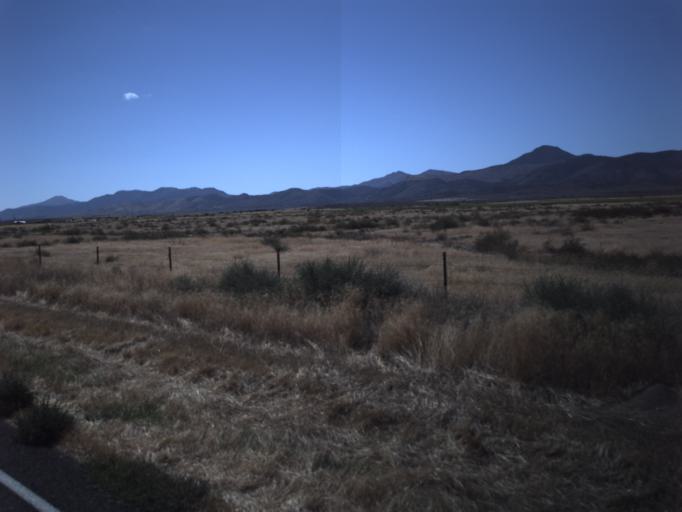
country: US
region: Utah
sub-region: Utah County
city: Genola
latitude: 40.0653
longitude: -111.9585
